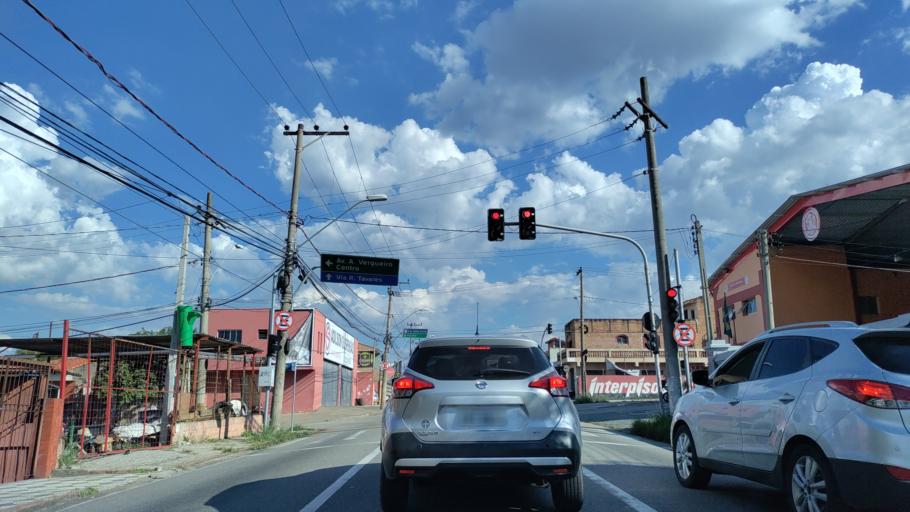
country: BR
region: Sao Paulo
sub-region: Sorocaba
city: Sorocaba
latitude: -23.5041
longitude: -47.4822
